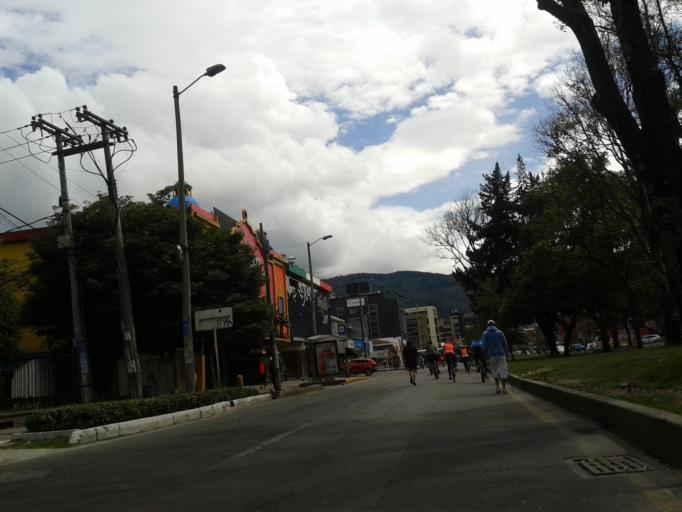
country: CO
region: Bogota D.C.
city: Barrio San Luis
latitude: 4.6989
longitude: -74.0513
